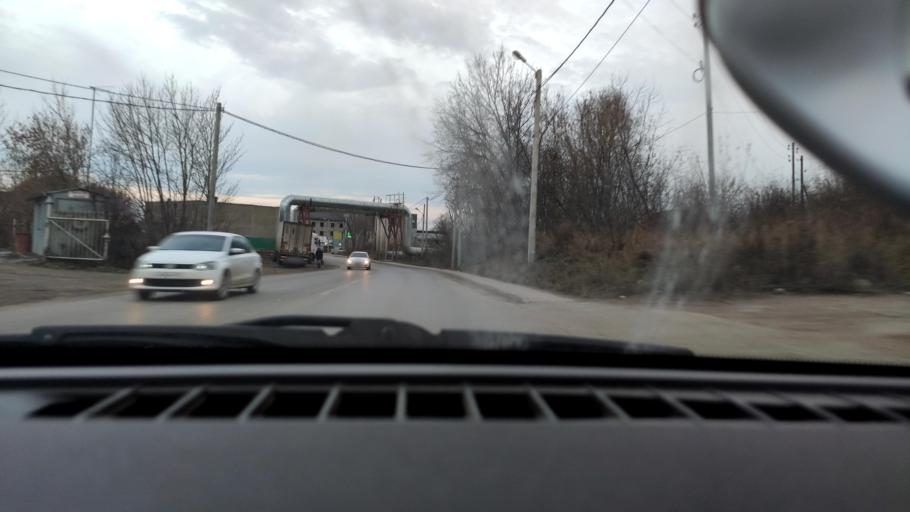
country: RU
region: Perm
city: Kondratovo
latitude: 57.9518
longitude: 56.1377
